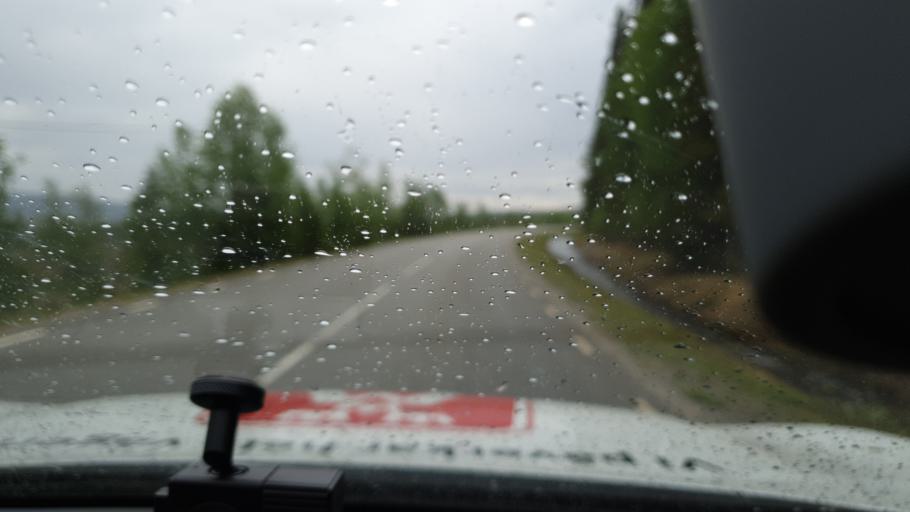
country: SE
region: Vaesterbotten
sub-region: Storumans Kommun
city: Fristad
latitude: 65.8581
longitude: 16.4731
